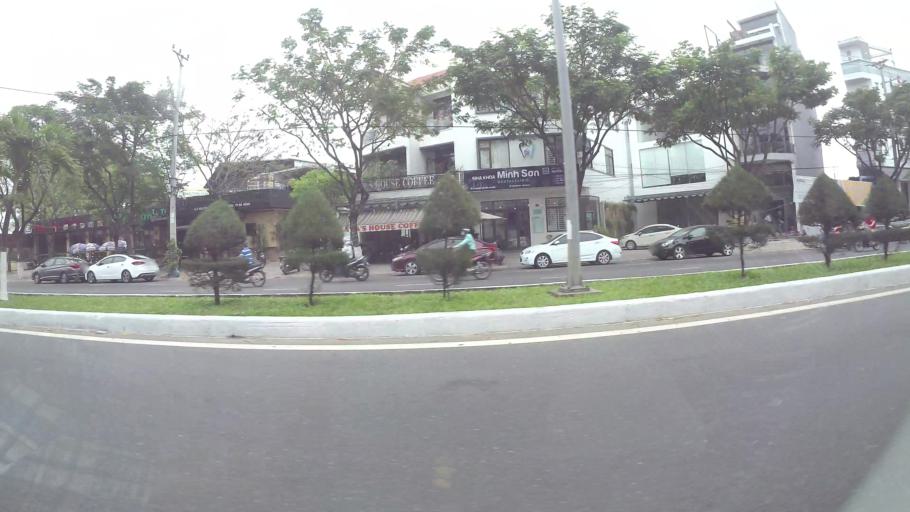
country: VN
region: Da Nang
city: Da Nang
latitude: 16.0480
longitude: 108.2094
